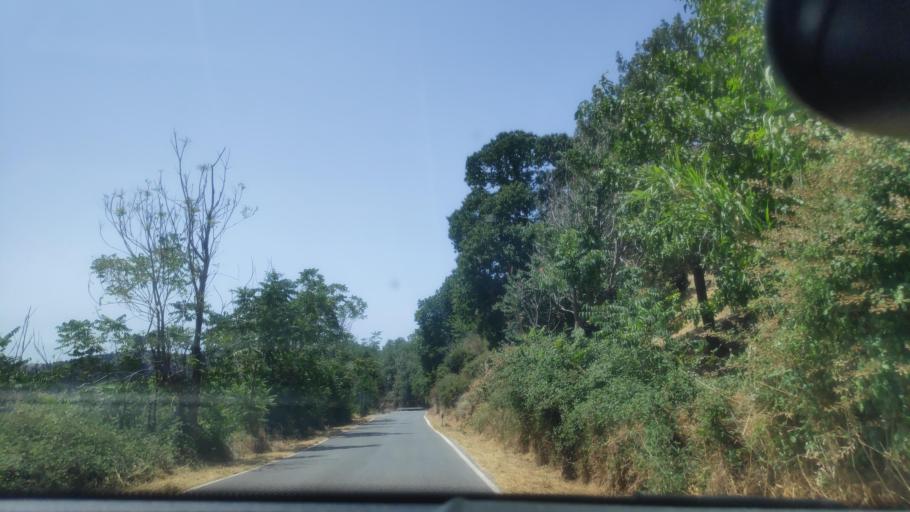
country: ES
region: Andalusia
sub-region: Provincia de Granada
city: Busquistar
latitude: 36.9596
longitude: -3.2785
